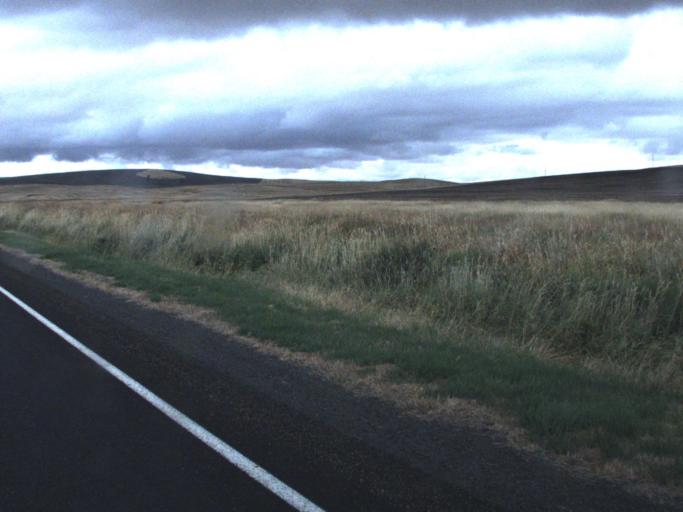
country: US
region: Washington
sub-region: Whitman County
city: Colfax
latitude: 47.1535
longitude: -117.2623
